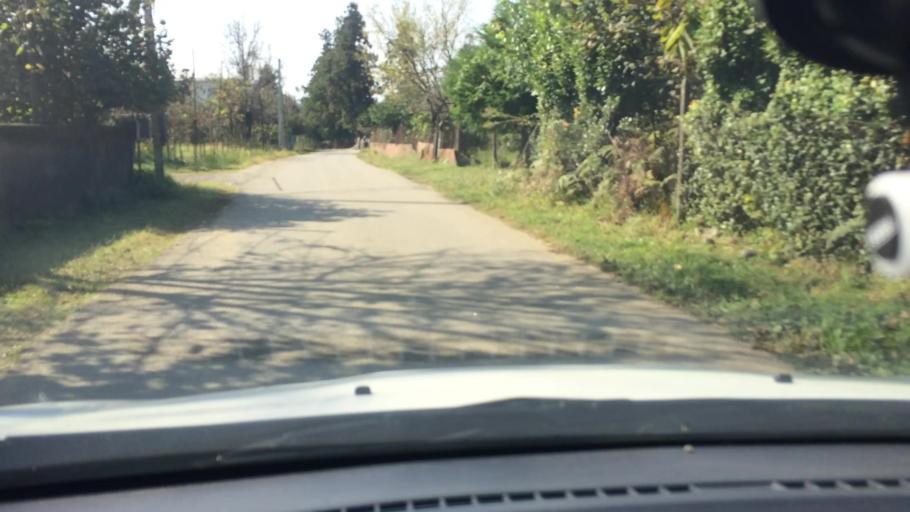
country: GE
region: Ajaria
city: Kobuleti
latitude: 41.8102
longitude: 41.8247
